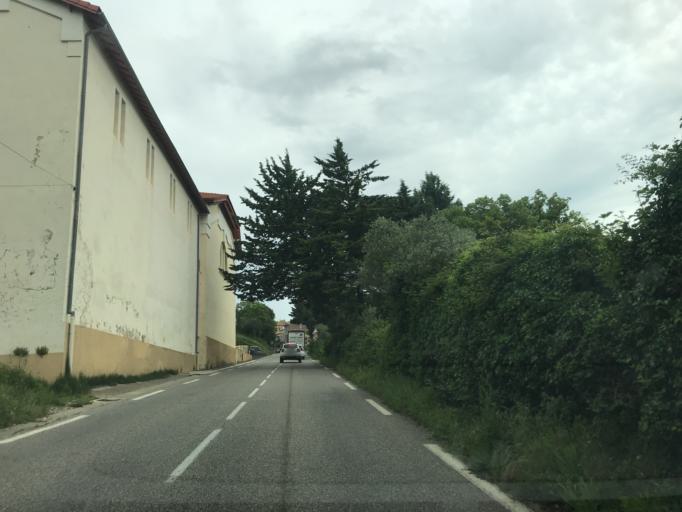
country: FR
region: Provence-Alpes-Cote d'Azur
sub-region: Departement du Var
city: Ginasservis
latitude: 43.6680
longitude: 5.8499
